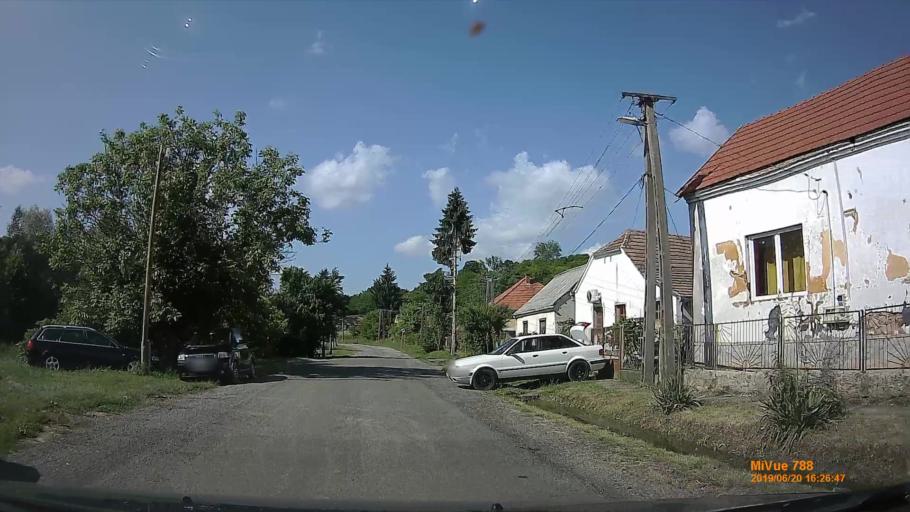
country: HU
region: Baranya
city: Buekkoesd
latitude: 46.1472
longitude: 18.0600
